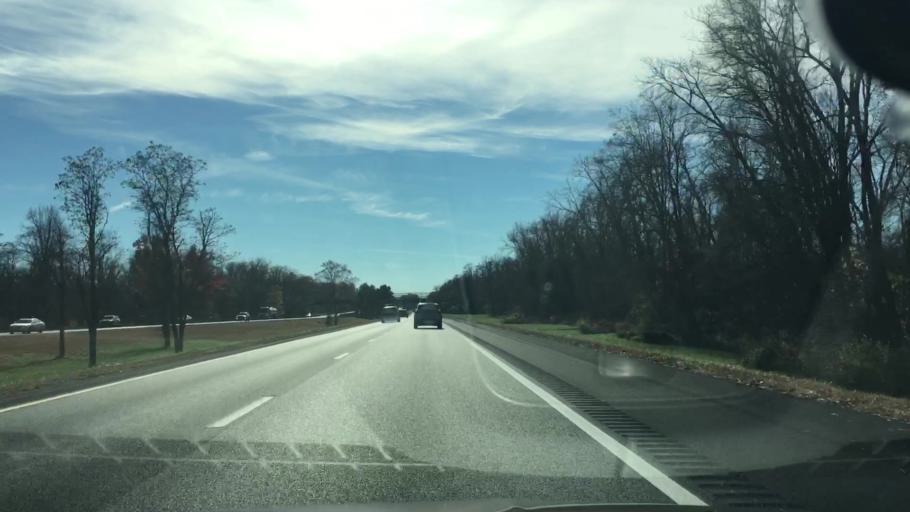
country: US
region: Massachusetts
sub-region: Franklin County
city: Whately
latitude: 42.4148
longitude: -72.6256
